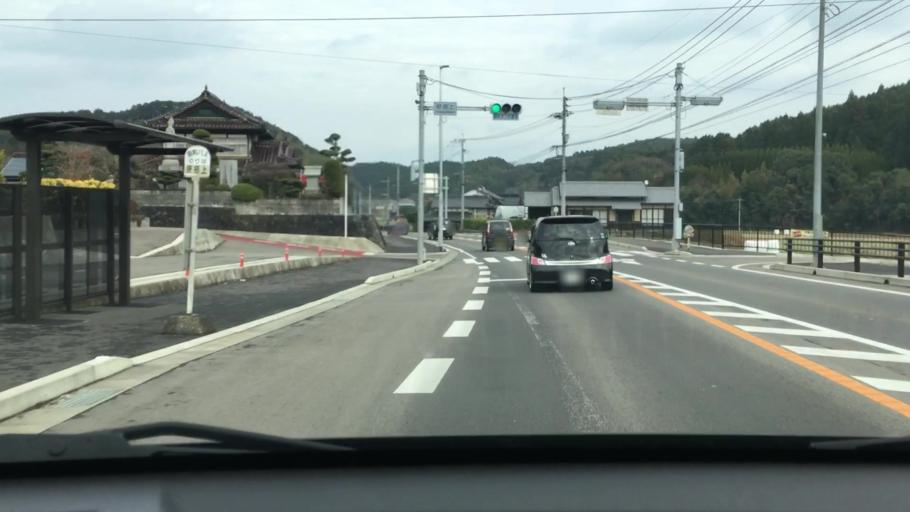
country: JP
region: Saga Prefecture
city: Imaricho-ko
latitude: 33.2948
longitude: 129.9138
